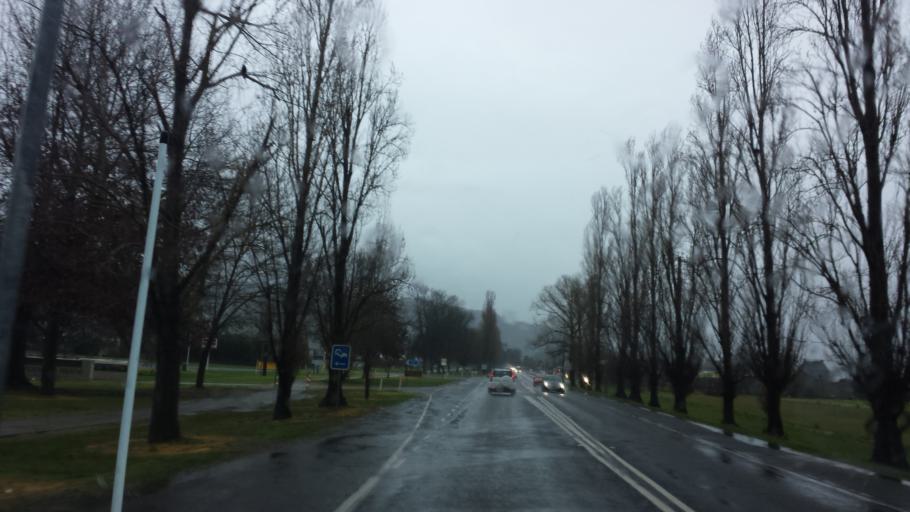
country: AU
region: Victoria
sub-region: Wangaratta
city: Wangaratta
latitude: -36.5544
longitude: 146.7133
